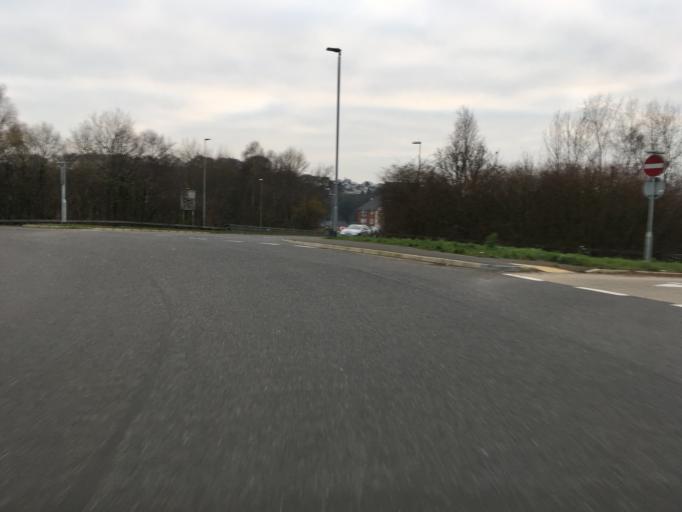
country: GB
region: Wales
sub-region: Caerphilly County Borough
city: Risca
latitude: 51.5859
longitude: -3.0528
